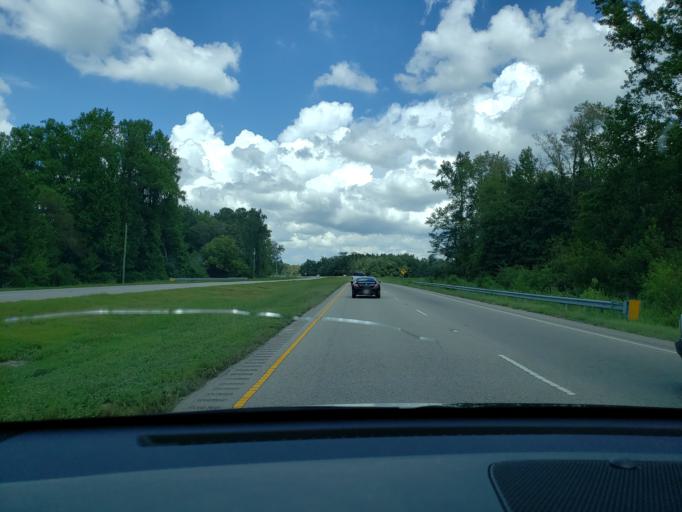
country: US
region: North Carolina
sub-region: Bladen County
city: Elizabethtown
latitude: 34.6991
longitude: -78.7397
